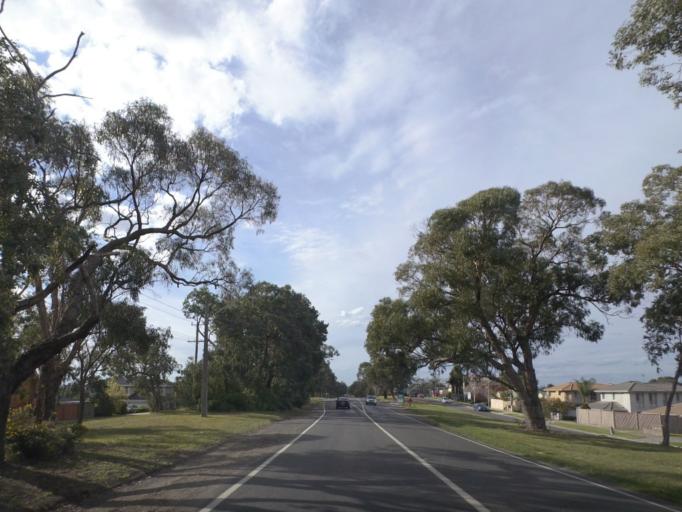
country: AU
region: Victoria
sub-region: Manningham
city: Donvale
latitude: -37.7716
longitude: 145.1702
